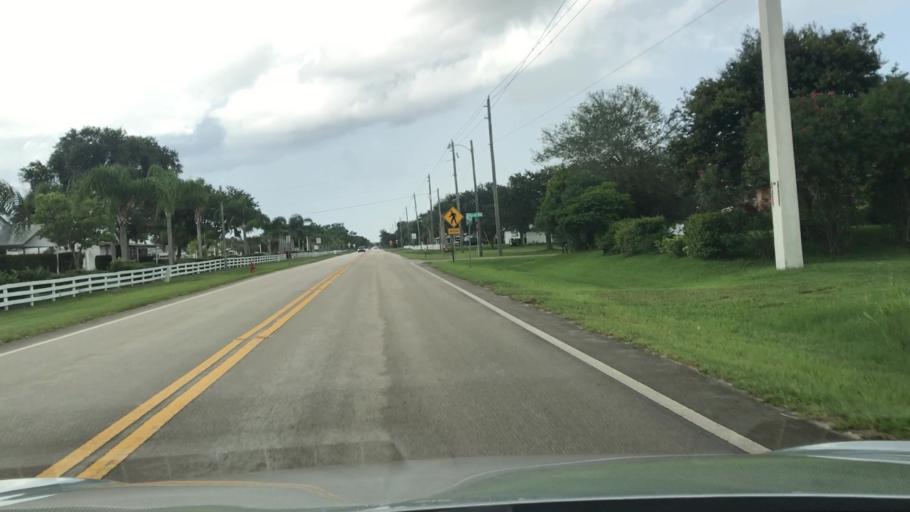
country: US
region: Florida
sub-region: Indian River County
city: Sebastian
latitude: 27.7895
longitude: -80.4991
